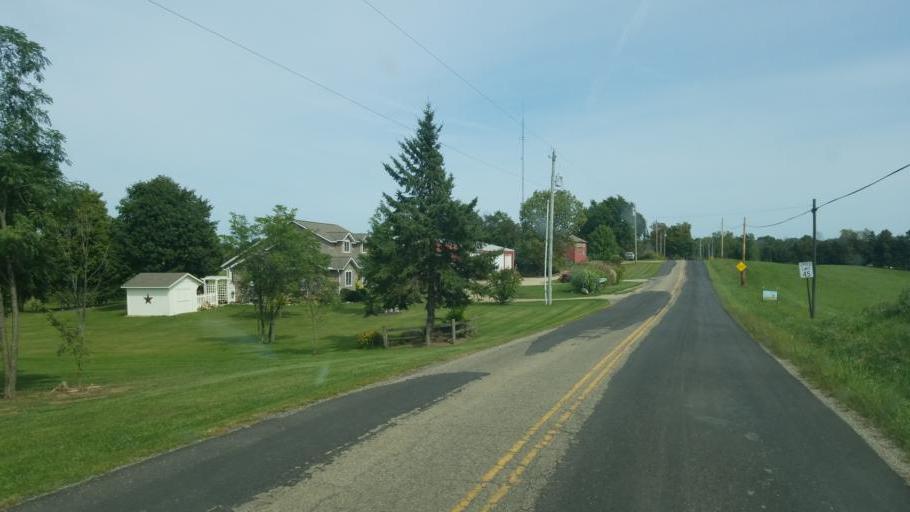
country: US
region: Ohio
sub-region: Knox County
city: Mount Vernon
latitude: 40.3786
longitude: -82.5786
